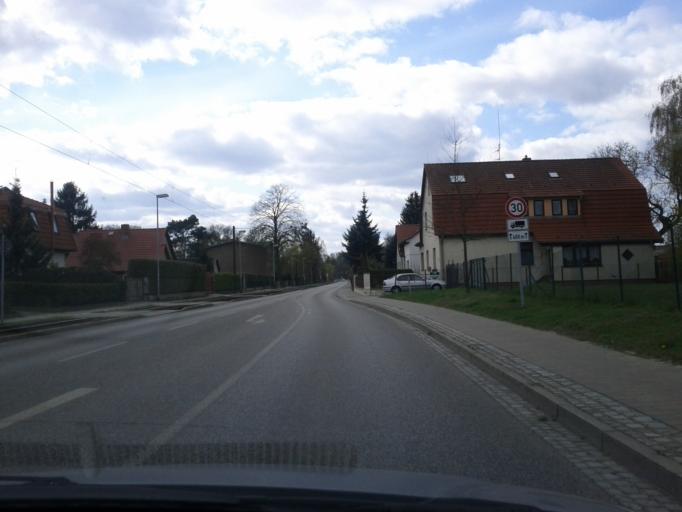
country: DE
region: Brandenburg
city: Schoneiche
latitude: 52.4778
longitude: 13.7080
